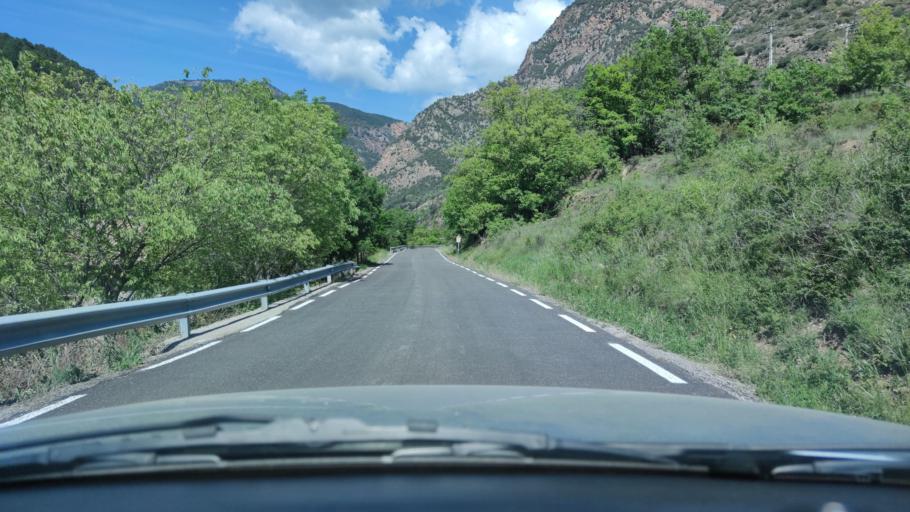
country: ES
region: Catalonia
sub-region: Provincia de Lleida
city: Coll de Nargo
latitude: 42.2947
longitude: 1.3141
